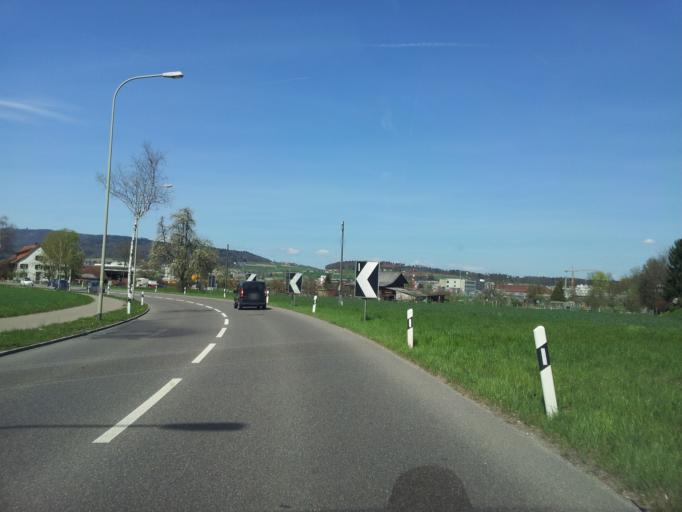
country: CH
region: Zurich
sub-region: Bezirk Dielsdorf
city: Regensdorf / Hofacher-Geeren
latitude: 47.4328
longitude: 8.4602
